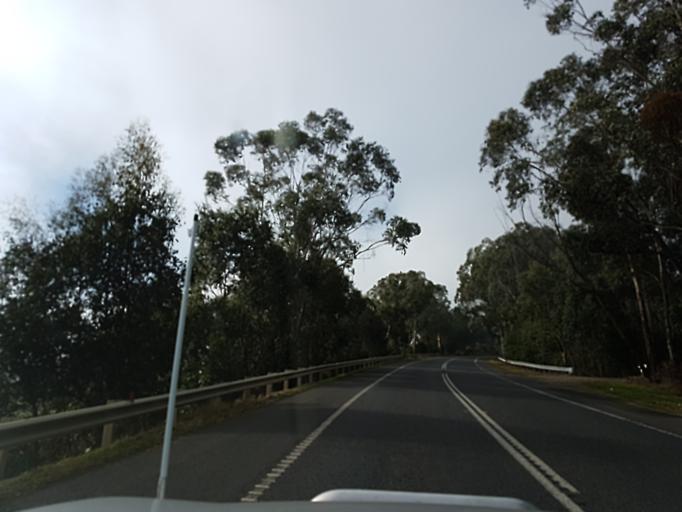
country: AU
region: Victoria
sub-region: Murrindindi
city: Kinglake West
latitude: -37.4156
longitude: 145.4353
